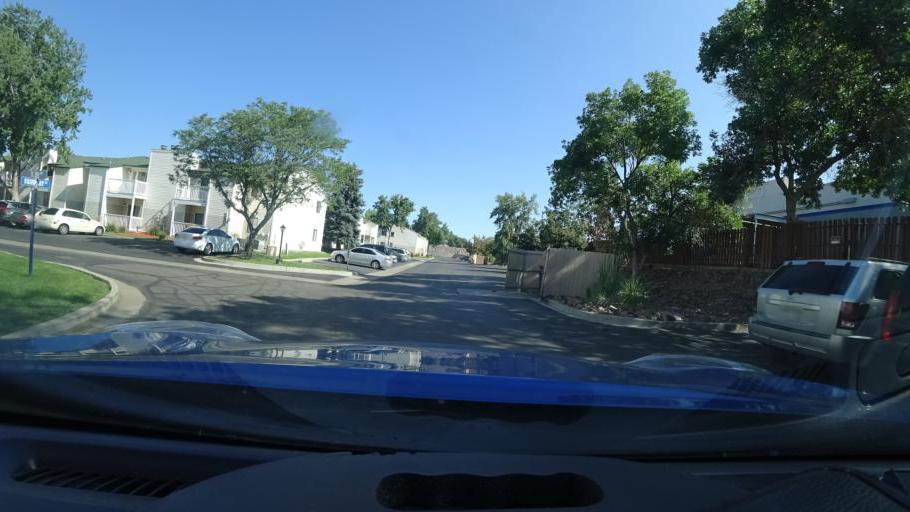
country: US
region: Colorado
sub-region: Adams County
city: Aurora
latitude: 39.7239
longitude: -104.8130
